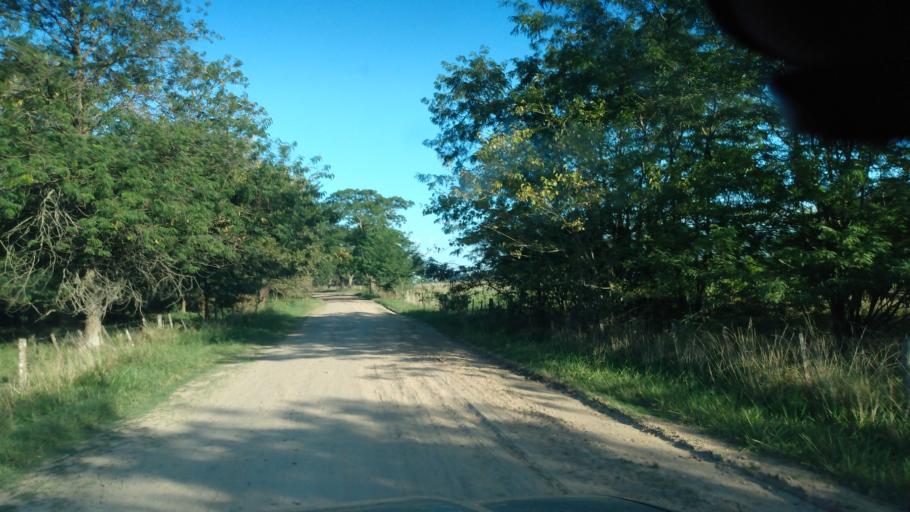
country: AR
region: Buenos Aires
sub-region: Partido de Lujan
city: Lujan
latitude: -34.5880
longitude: -59.0658
